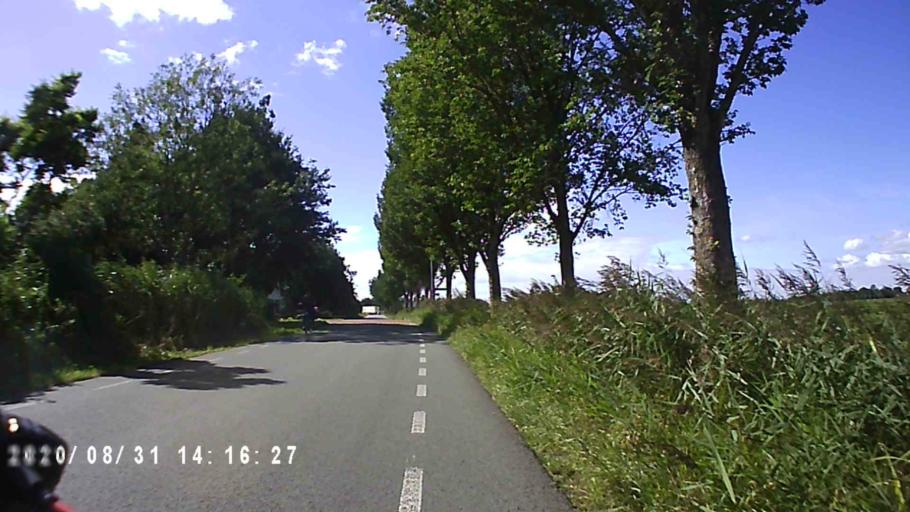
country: NL
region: Groningen
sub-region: Gemeente Zuidhorn
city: Aduard
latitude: 53.2054
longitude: 6.4511
